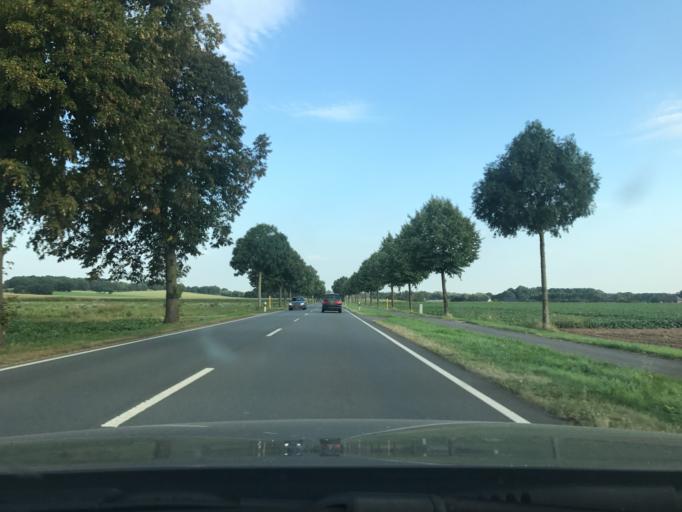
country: DE
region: North Rhine-Westphalia
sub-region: Regierungsbezirk Dusseldorf
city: Rheurdt
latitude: 51.4193
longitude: 6.4653
